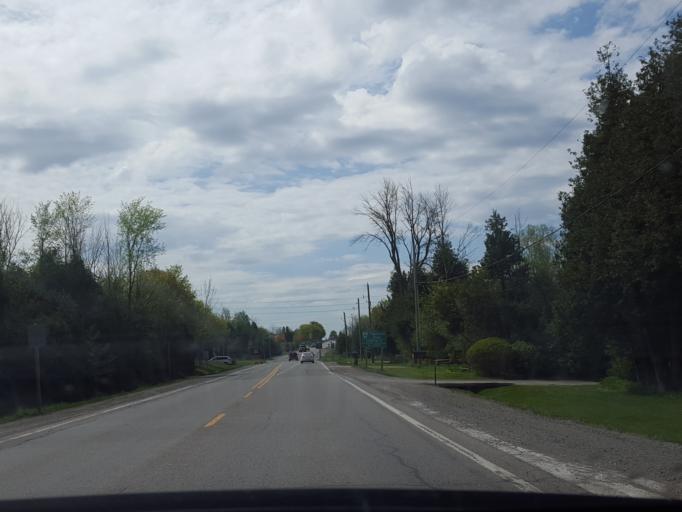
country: CA
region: Ontario
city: Oshawa
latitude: 43.9699
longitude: -78.7283
